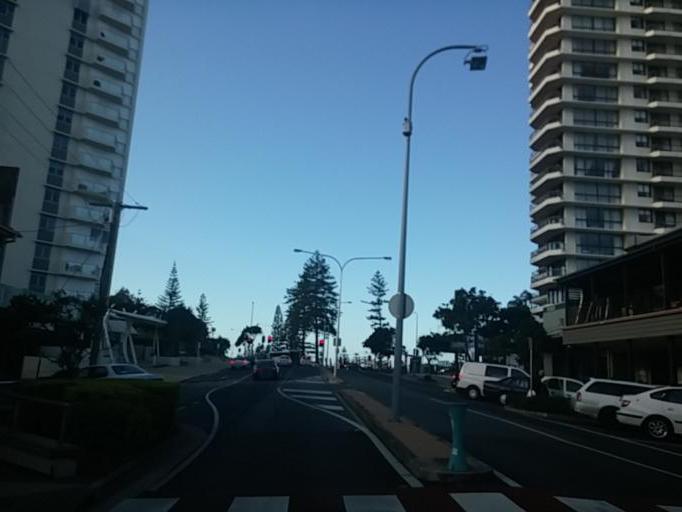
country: AU
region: New South Wales
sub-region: Tweed
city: Tweed Heads West
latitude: -28.1679
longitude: 153.5354
